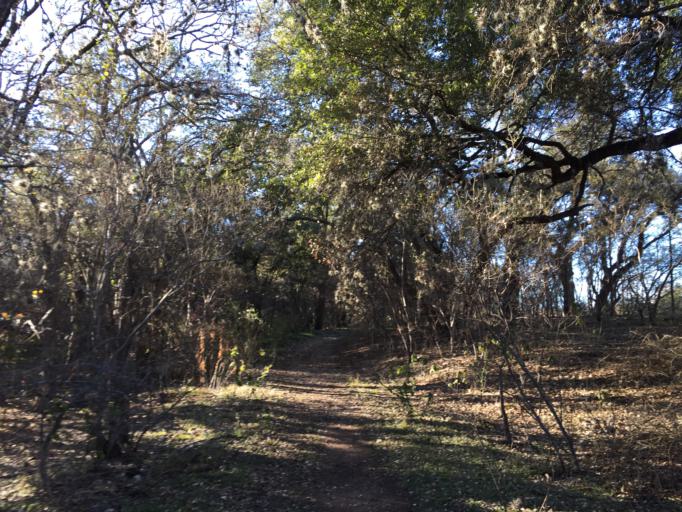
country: US
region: Texas
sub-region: Bexar County
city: Castle Hills
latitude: 29.5592
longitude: -98.5026
